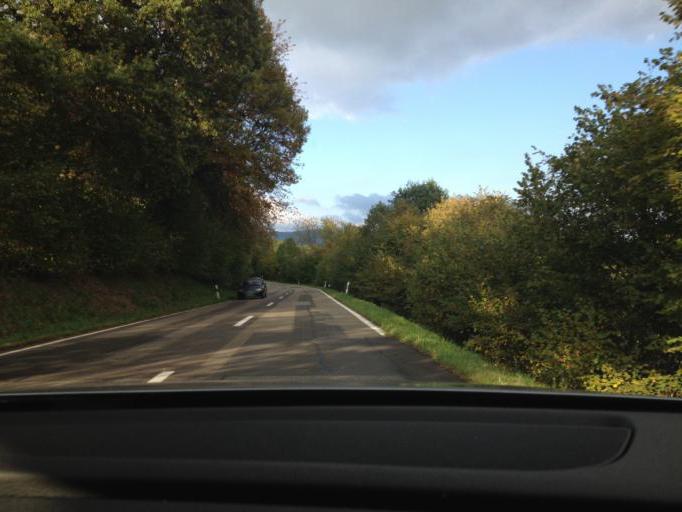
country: DE
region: Saarland
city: Freisen
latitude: 49.5132
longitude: 7.2467
